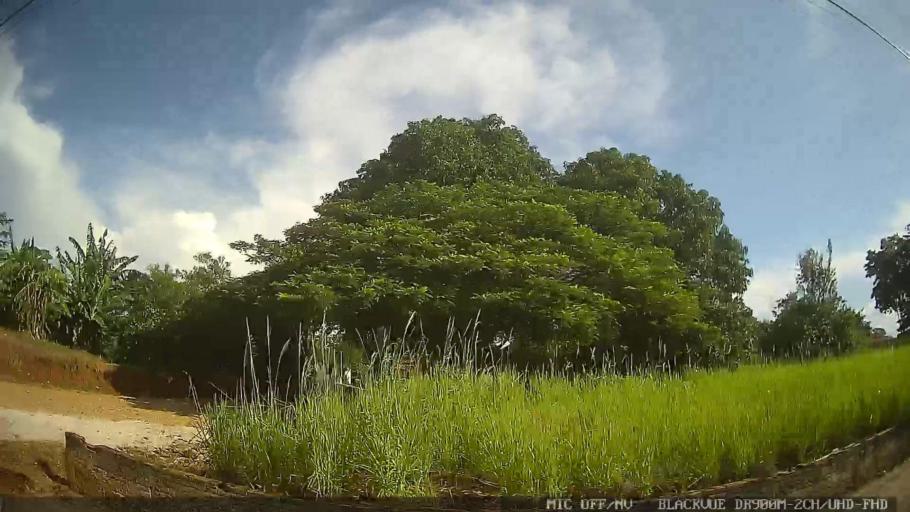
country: BR
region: Sao Paulo
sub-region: Laranjal Paulista
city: Laranjal Paulista
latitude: -23.0855
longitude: -47.7928
